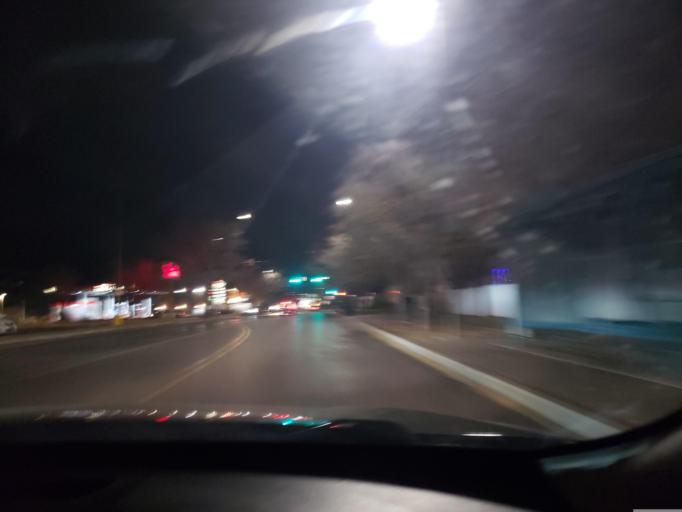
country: US
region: New Mexico
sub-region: Bernalillo County
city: Albuquerque
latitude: 35.0759
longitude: -106.6222
